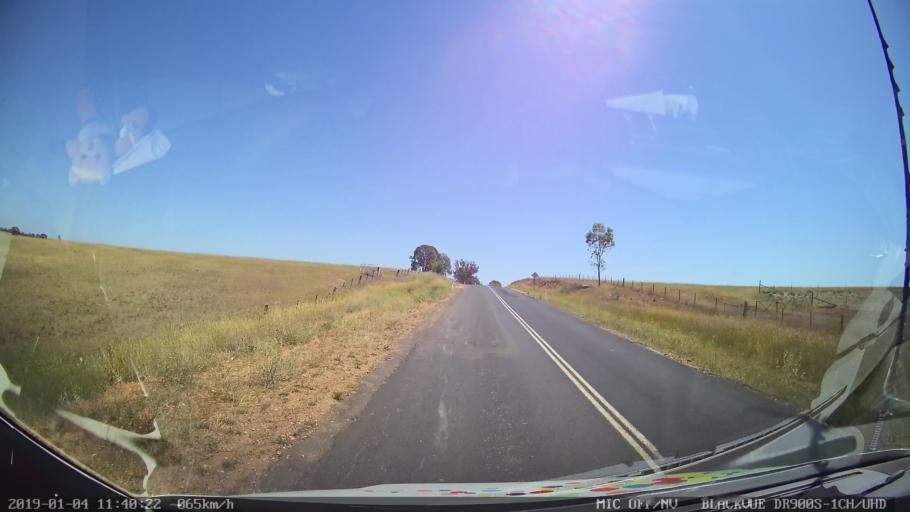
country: AU
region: New South Wales
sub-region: Cabonne
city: Molong
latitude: -33.0056
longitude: 148.7875
